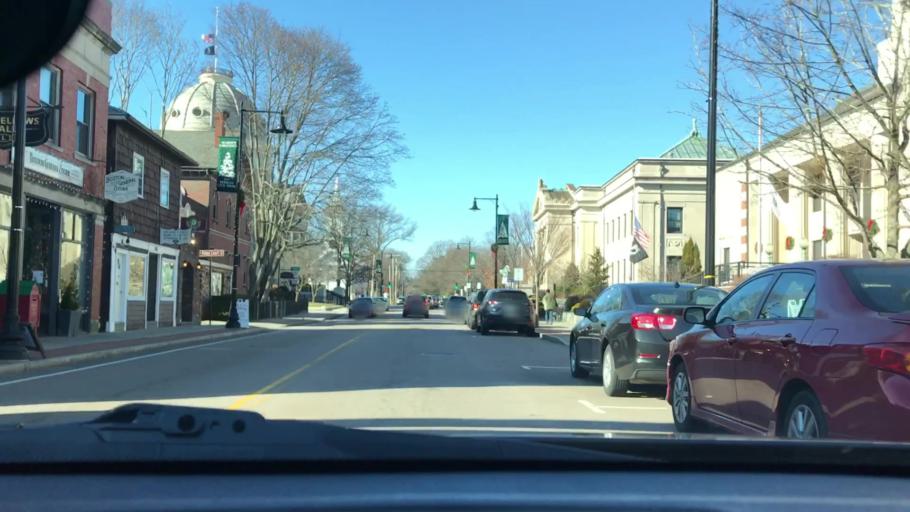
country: US
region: Massachusetts
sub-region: Norfolk County
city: Dedham
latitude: 42.2486
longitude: -71.1748
